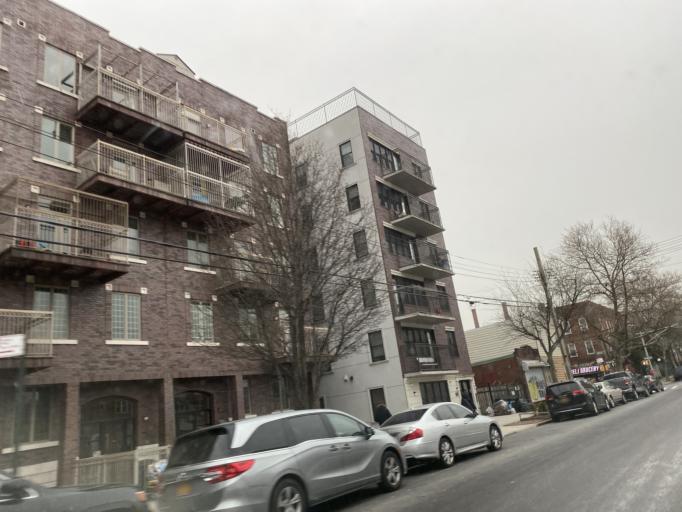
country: US
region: New York
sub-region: Kings County
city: Brooklyn
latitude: 40.6611
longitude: -73.9455
